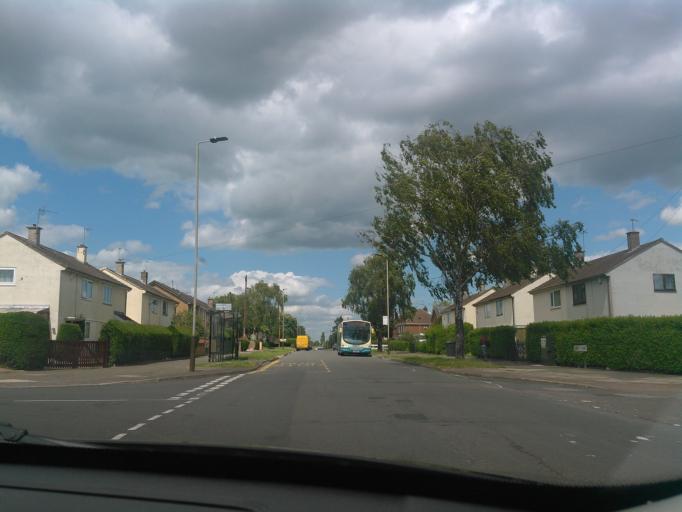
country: GB
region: England
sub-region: Leicestershire
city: Glenfield
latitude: 52.6392
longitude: -1.1928
